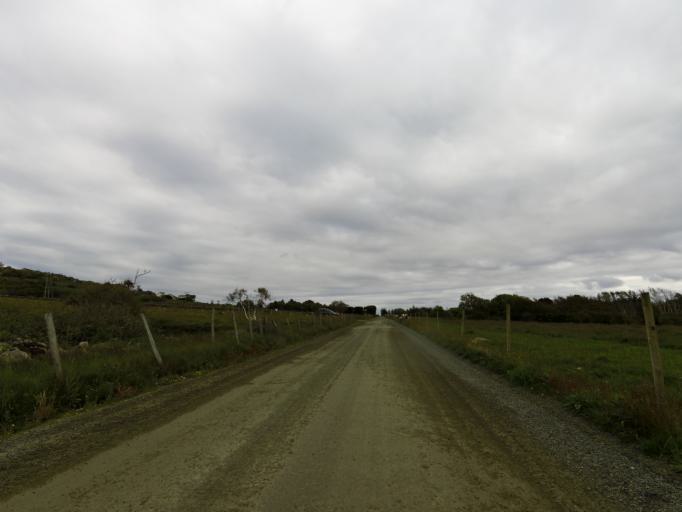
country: NO
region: Vest-Agder
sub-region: Farsund
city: Vestbygd
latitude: 58.1317
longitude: 6.6100
